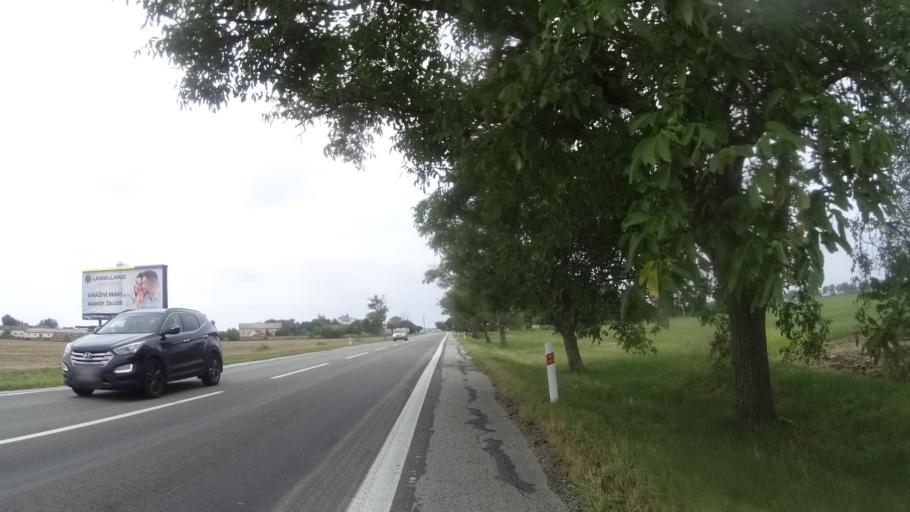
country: HU
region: Komarom-Esztergom
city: Acs
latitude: 47.7667
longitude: 18.0215
